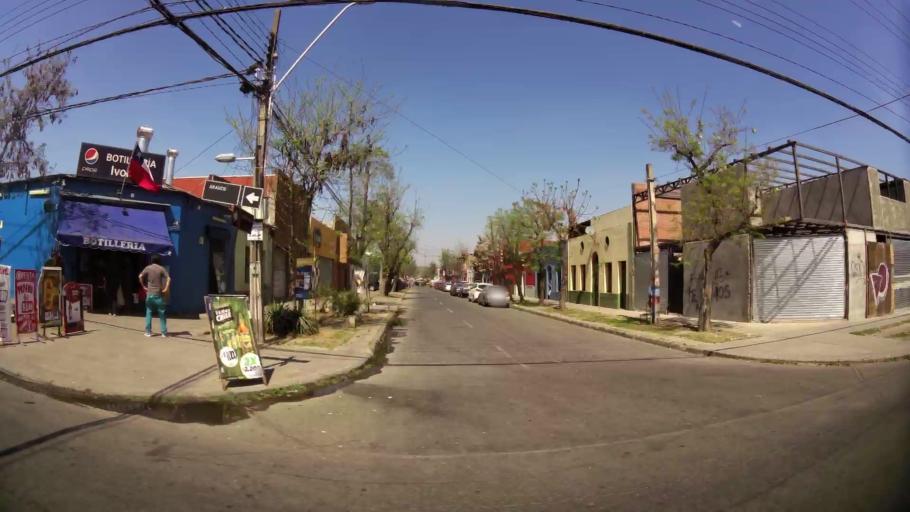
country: CL
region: Santiago Metropolitan
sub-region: Provincia de Santiago
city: Santiago
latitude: -33.4716
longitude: -70.6408
